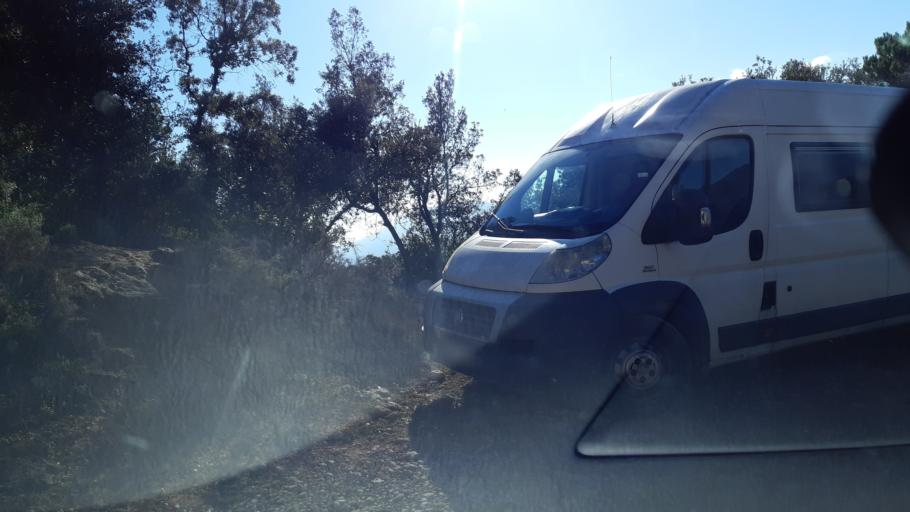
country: ES
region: Catalonia
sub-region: Provincia de Girona
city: la Cellera de Ter
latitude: 42.0204
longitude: 2.6081
